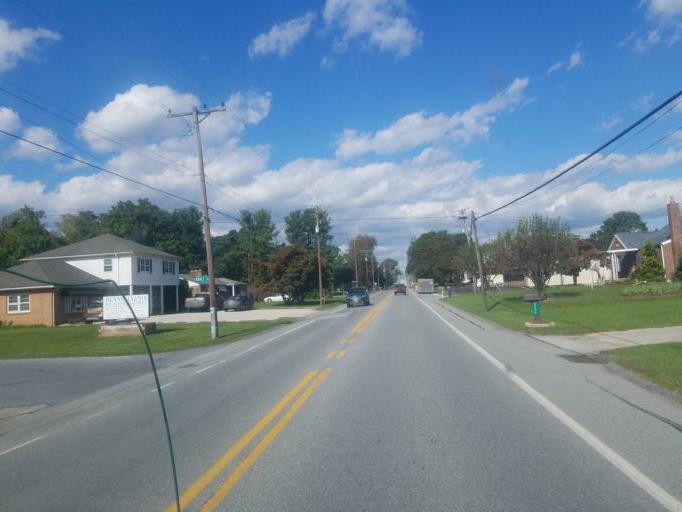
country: US
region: Pennsylvania
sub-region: York County
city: Emigsville
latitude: 40.0015
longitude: -76.7337
